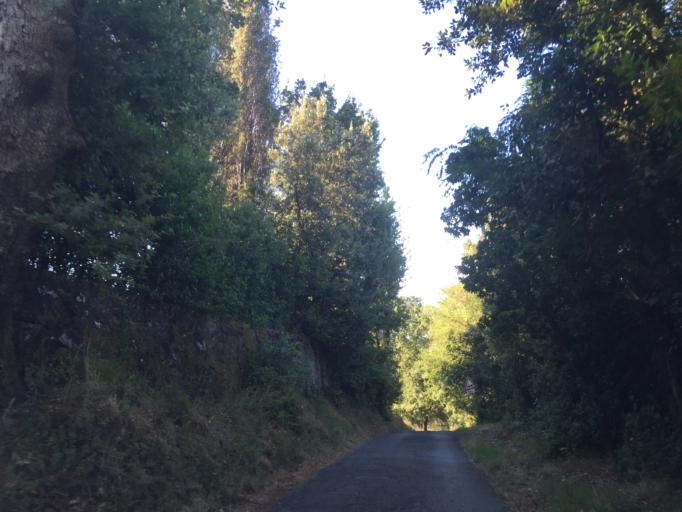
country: IT
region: Tuscany
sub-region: Provincia di Pistoia
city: Pistoia
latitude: 43.9594
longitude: 10.9407
